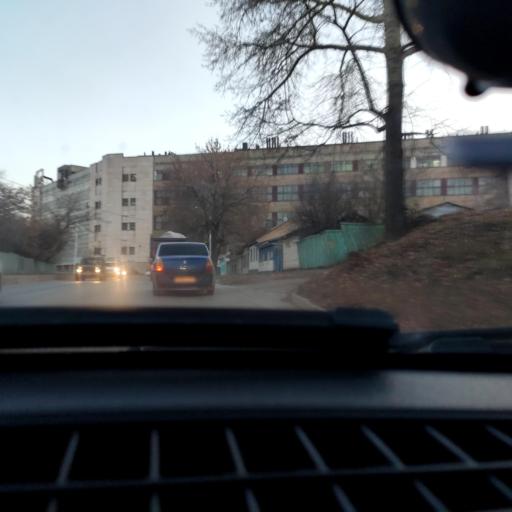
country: RU
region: Bashkortostan
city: Ufa
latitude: 54.7397
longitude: 55.9388
